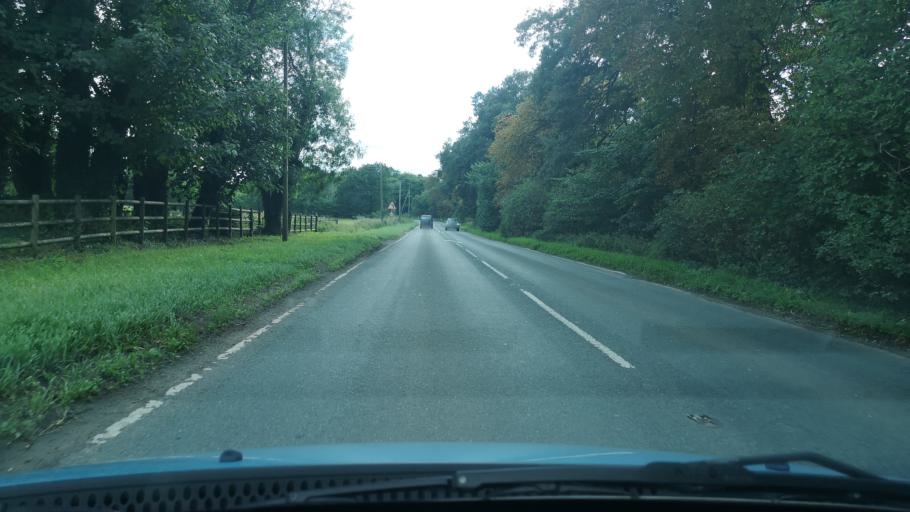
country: GB
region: England
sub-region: North Lincolnshire
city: Crowle
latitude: 53.5817
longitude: -0.8206
